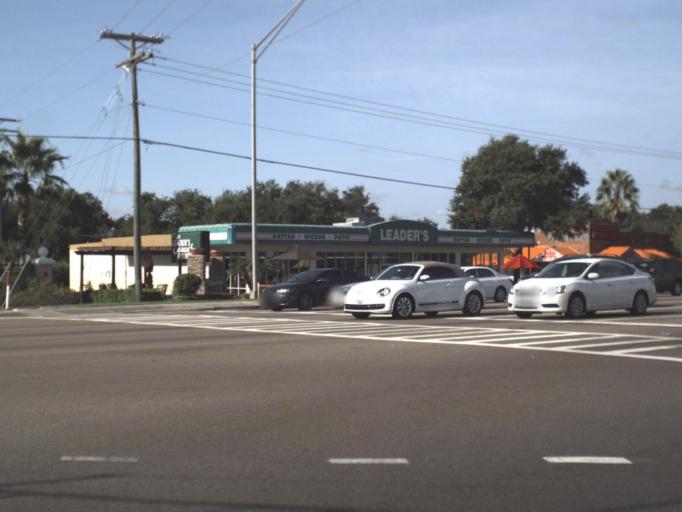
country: US
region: Florida
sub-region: Hillsborough County
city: Brandon
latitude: 27.9378
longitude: -82.3104
